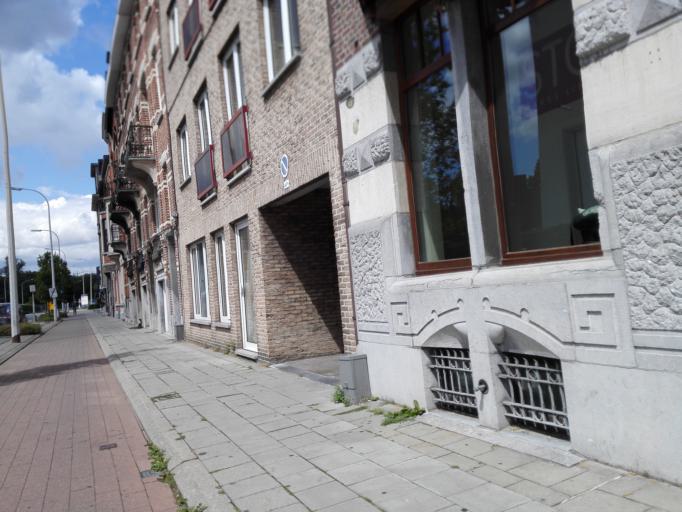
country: BE
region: Flanders
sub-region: Provincie Vlaams-Brabant
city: Leuven
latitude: 50.8693
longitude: 4.6969
